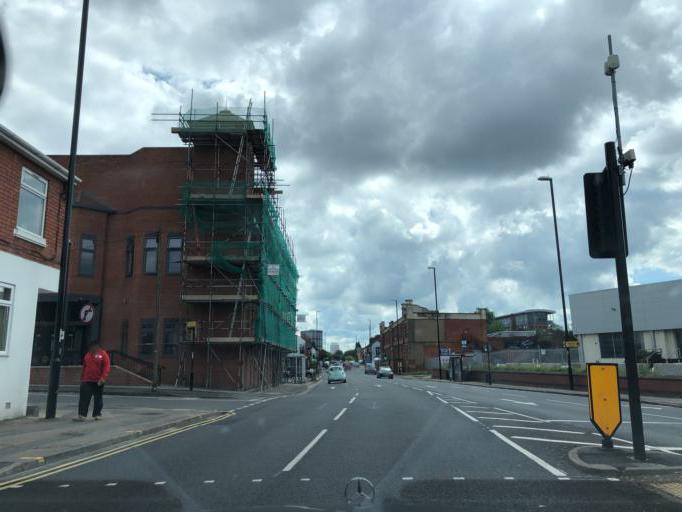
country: GB
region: England
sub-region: Coventry
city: Coventry
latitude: 52.4213
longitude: -1.5055
